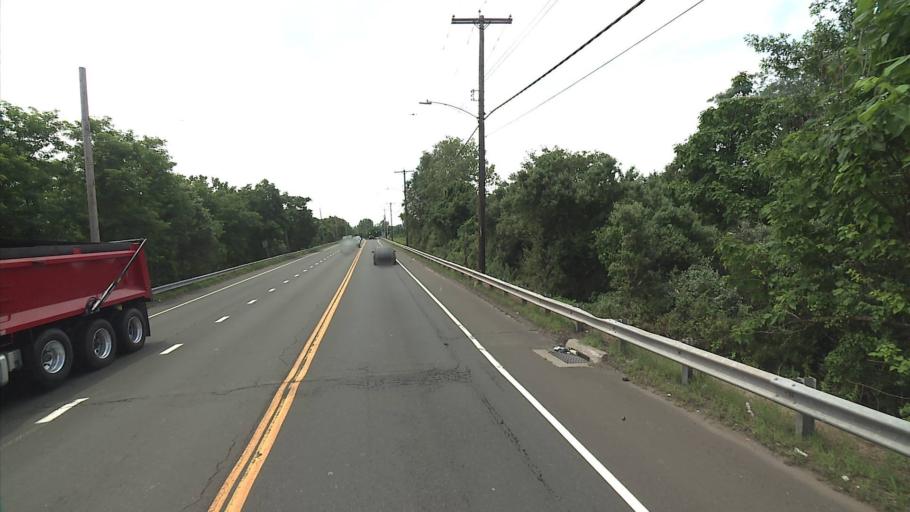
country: US
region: Connecticut
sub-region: New Haven County
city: New Haven
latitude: 41.3261
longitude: -72.8802
